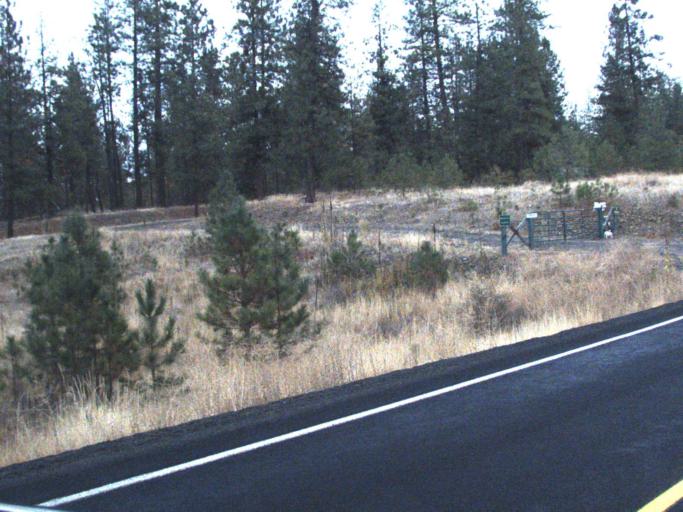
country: US
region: Washington
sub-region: Lincoln County
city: Davenport
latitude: 47.8242
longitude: -118.1970
